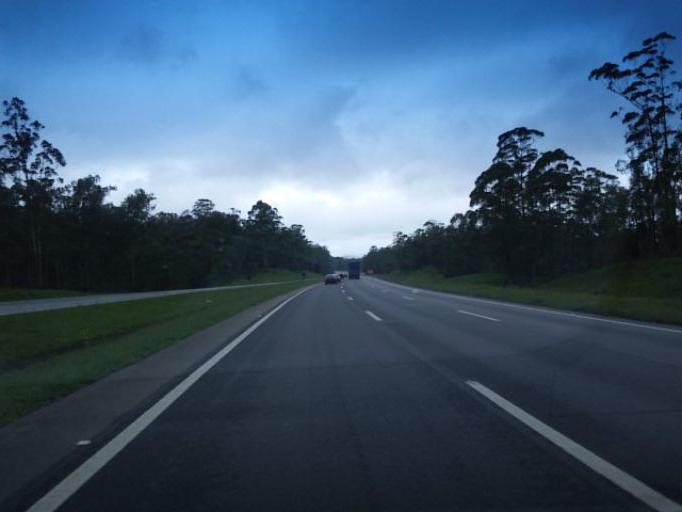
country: BR
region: Parana
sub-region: Piraquara
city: Piraquara
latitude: -25.4339
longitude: -49.0881
